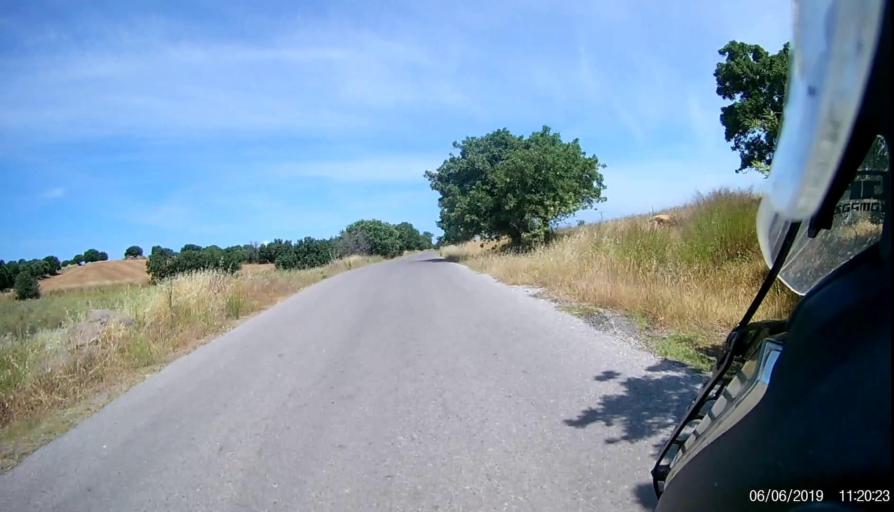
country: TR
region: Canakkale
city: Gulpinar
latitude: 39.6658
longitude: 26.1636
